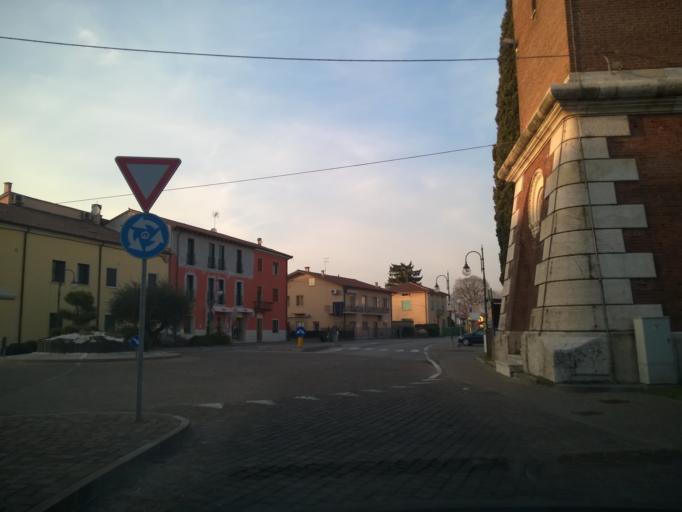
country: IT
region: Veneto
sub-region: Provincia di Vicenza
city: Caldogno-Rettorgole-Cresole
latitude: 45.6151
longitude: 11.5065
